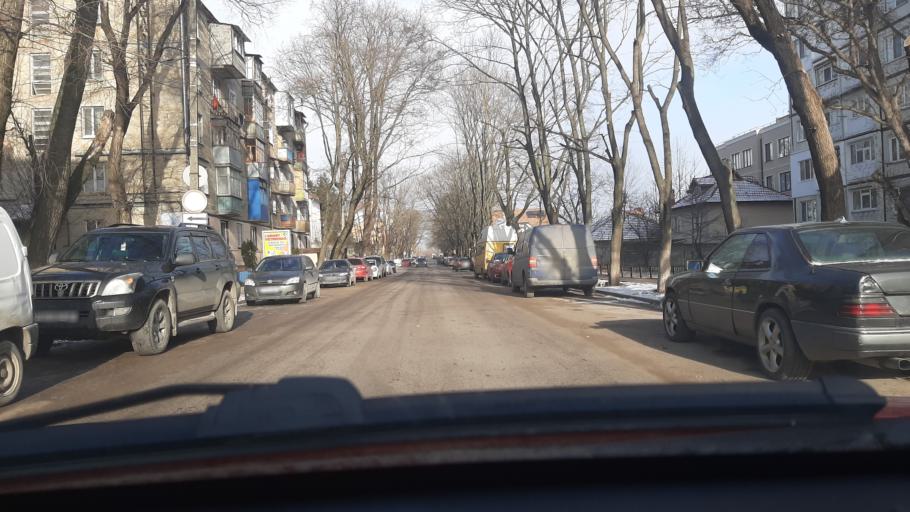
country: MD
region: Chisinau
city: Chisinau
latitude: 47.0025
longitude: 28.8151
